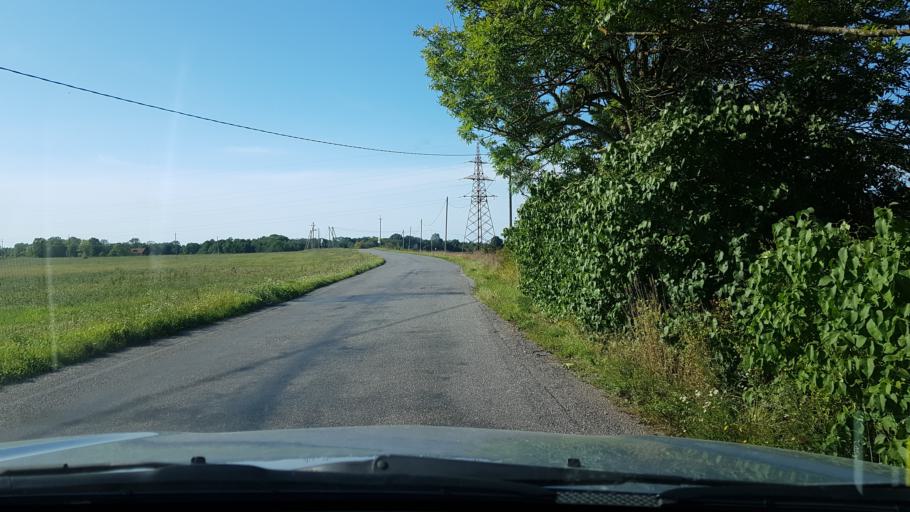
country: EE
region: Ida-Virumaa
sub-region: Narva-Joesuu linn
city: Narva-Joesuu
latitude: 59.4075
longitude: 28.0298
